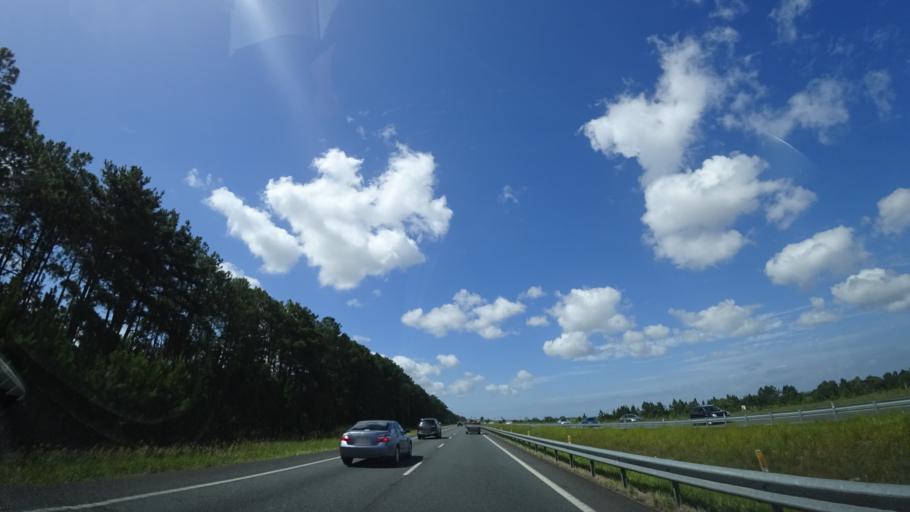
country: AU
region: Queensland
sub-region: Sunshine Coast
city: Little Mountain
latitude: -26.8345
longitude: 153.0329
